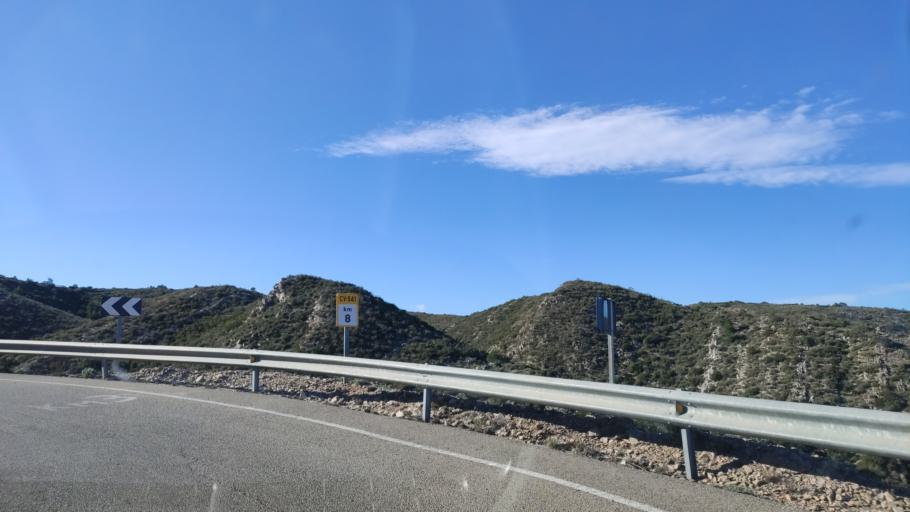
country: ES
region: Valencia
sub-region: Provincia de Valencia
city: Tous
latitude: 39.1382
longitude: -0.6094
